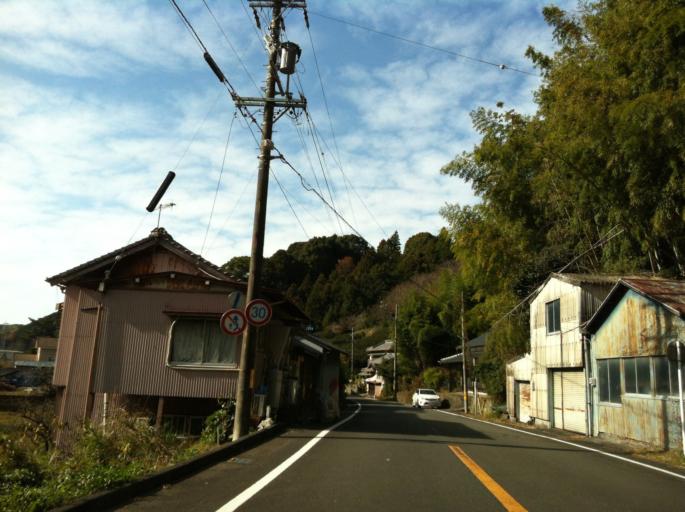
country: JP
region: Shizuoka
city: Yaizu
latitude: 34.9251
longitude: 138.2997
